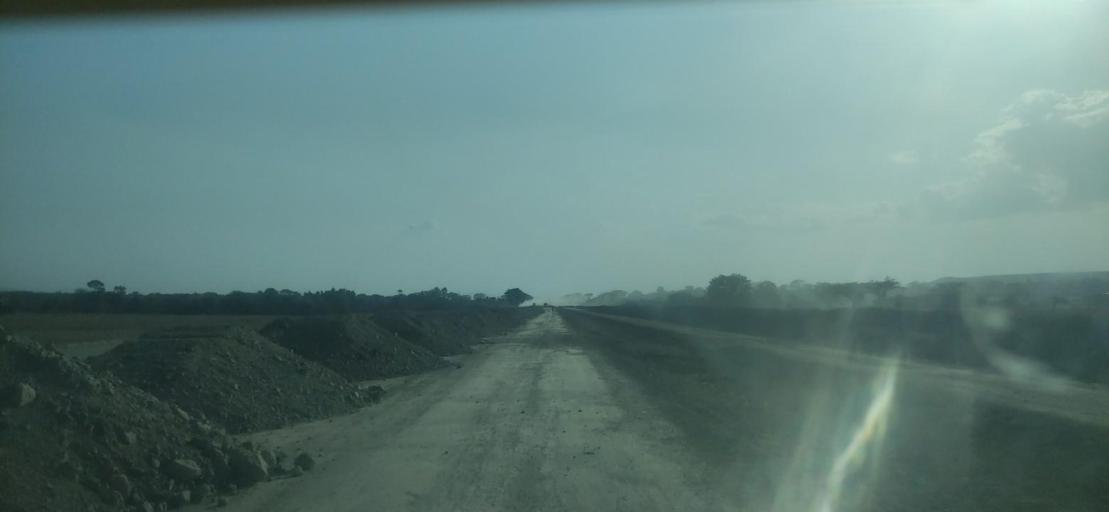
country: ET
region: Southern Nations, Nationalities, and People's Region
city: Hawassa
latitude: 7.1618
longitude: 38.4836
